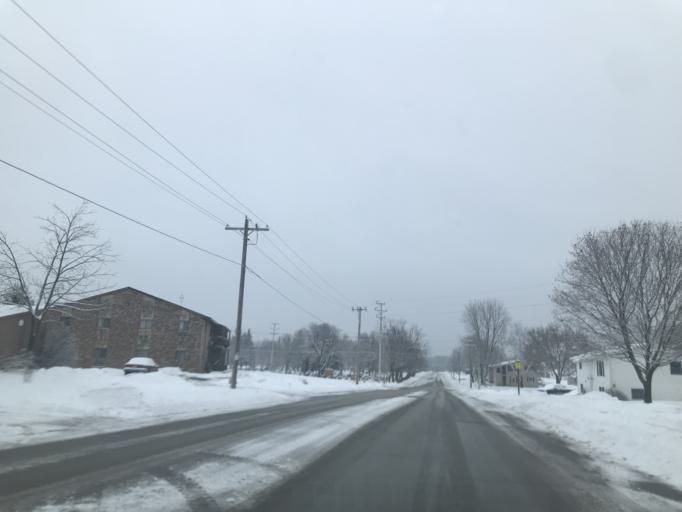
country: US
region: Wisconsin
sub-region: Oconto County
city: Oconto Falls
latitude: 44.8686
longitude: -88.1317
